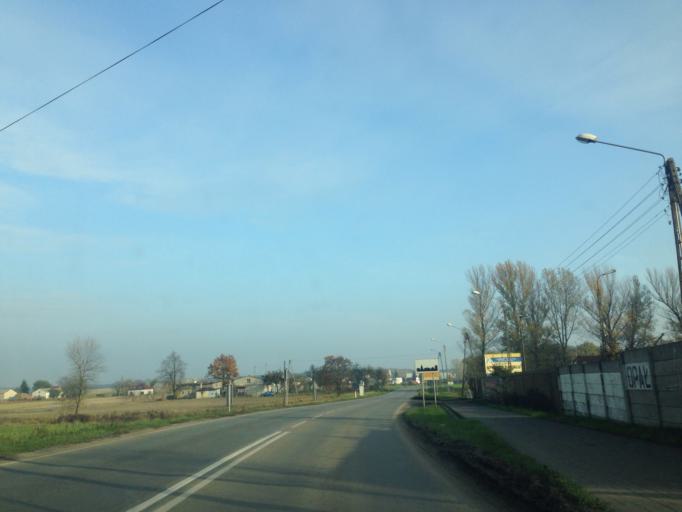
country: PL
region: Kujawsko-Pomorskie
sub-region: Powiat wabrzeski
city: Wabrzezno
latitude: 53.2669
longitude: 18.9839
